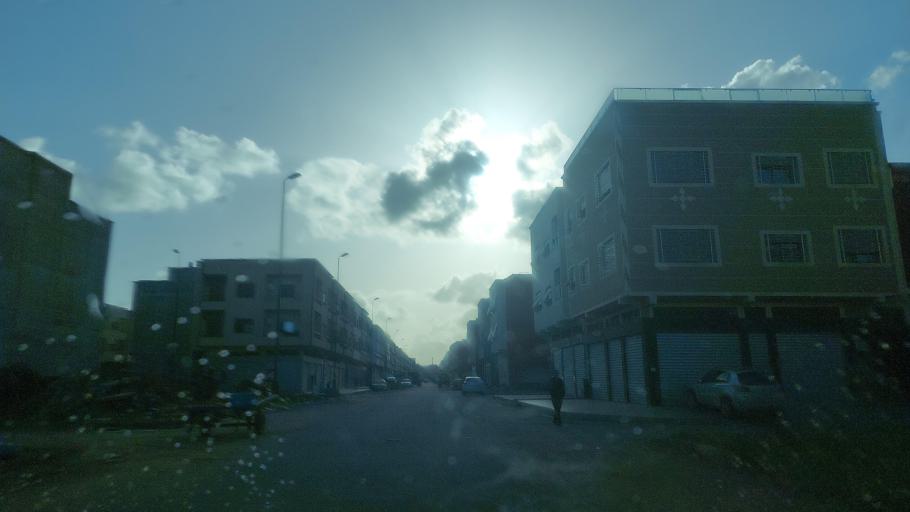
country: MA
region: Grand Casablanca
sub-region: Mediouna
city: Mediouna
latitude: 33.3773
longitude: -7.5284
